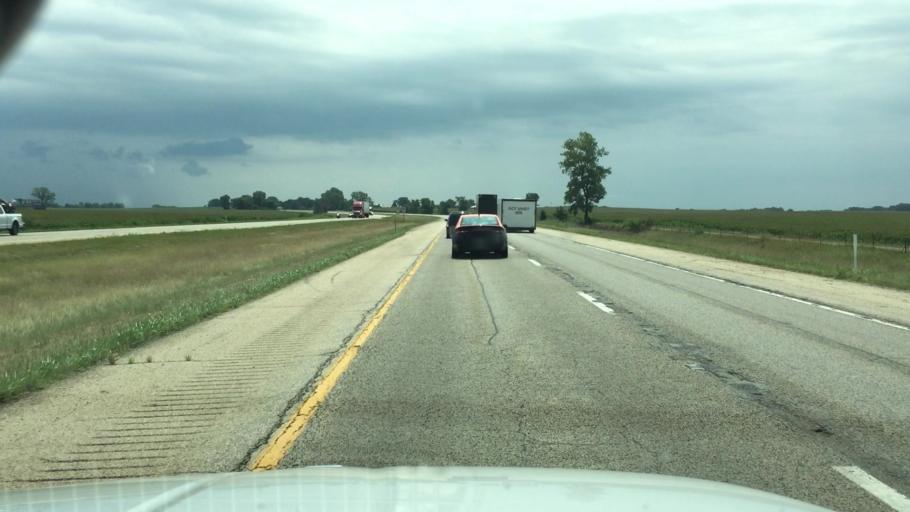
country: US
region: Illinois
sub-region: Peoria County
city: Elmwood
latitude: 40.8221
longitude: -89.8613
